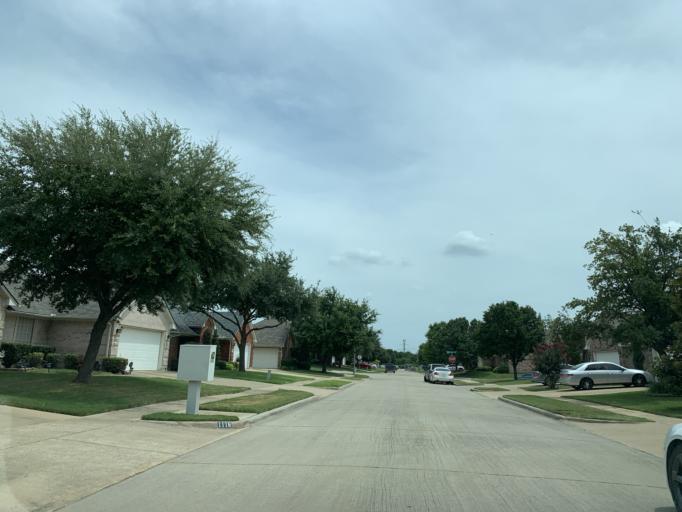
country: US
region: Texas
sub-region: Dallas County
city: Grand Prairie
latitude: 32.6604
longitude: -97.0218
